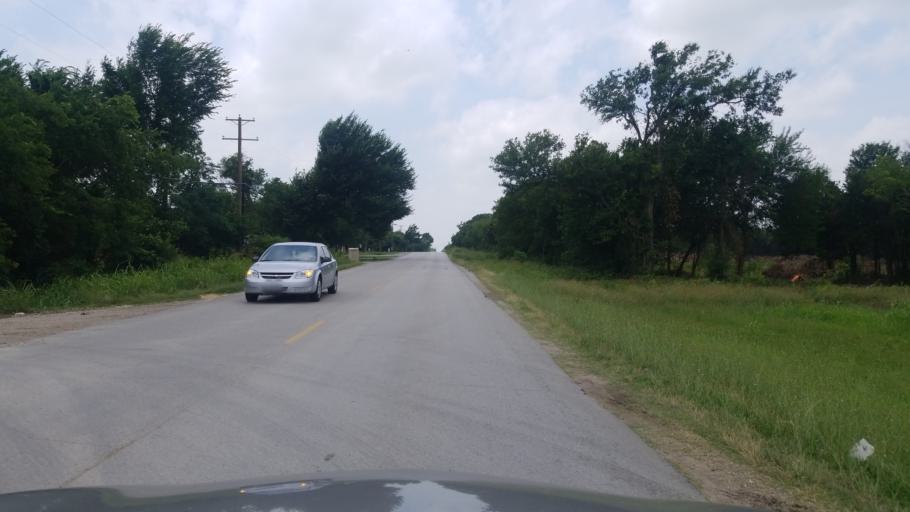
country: US
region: Texas
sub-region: Dallas County
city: Duncanville
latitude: 32.6912
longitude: -96.9112
